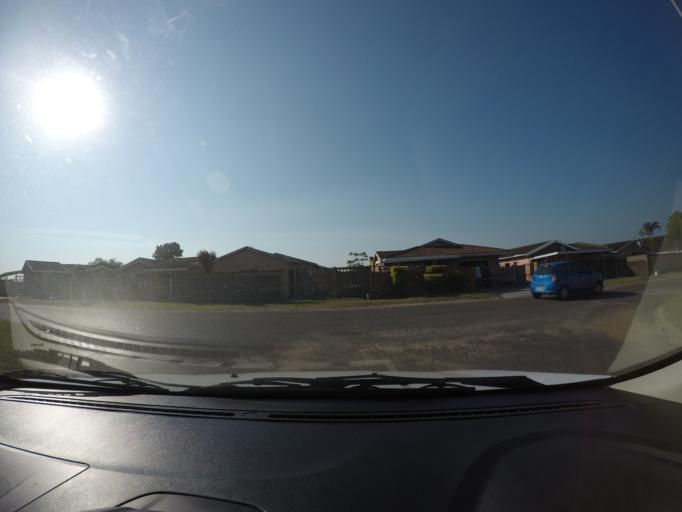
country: ZA
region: KwaZulu-Natal
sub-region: uThungulu District Municipality
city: Richards Bay
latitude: -28.7134
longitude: 32.0397
